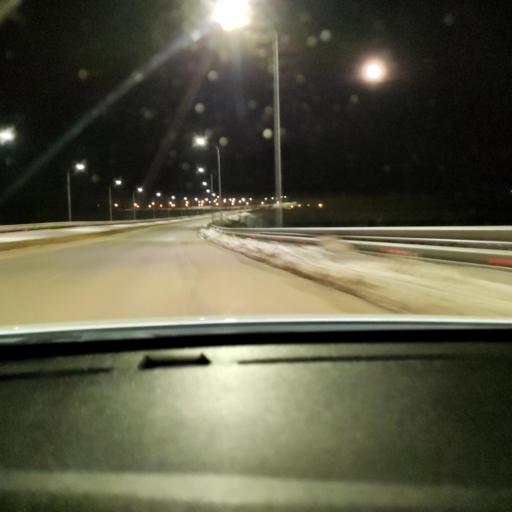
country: RU
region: Tatarstan
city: Sviyazhsk
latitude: 55.7459
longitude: 48.7682
